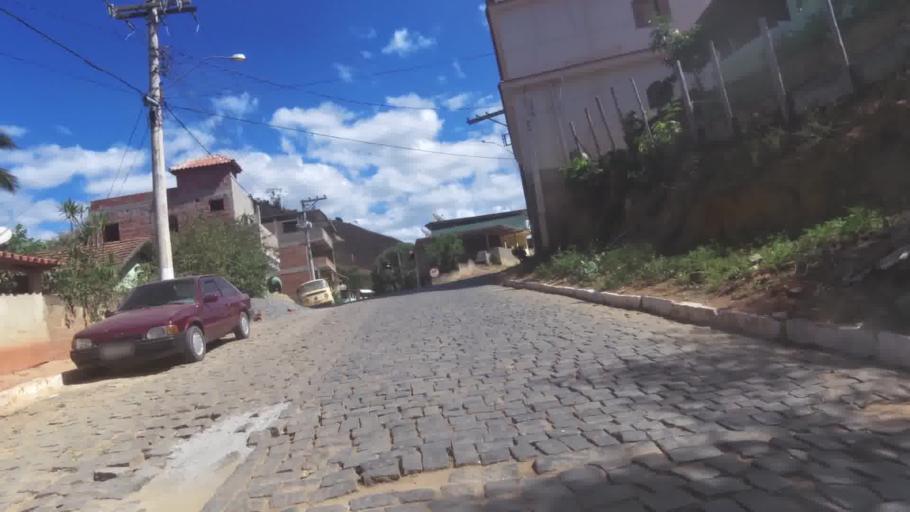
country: BR
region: Espirito Santo
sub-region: Cachoeiro De Itapemirim
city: Cachoeiro de Itapemirim
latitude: -20.9150
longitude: -41.1985
